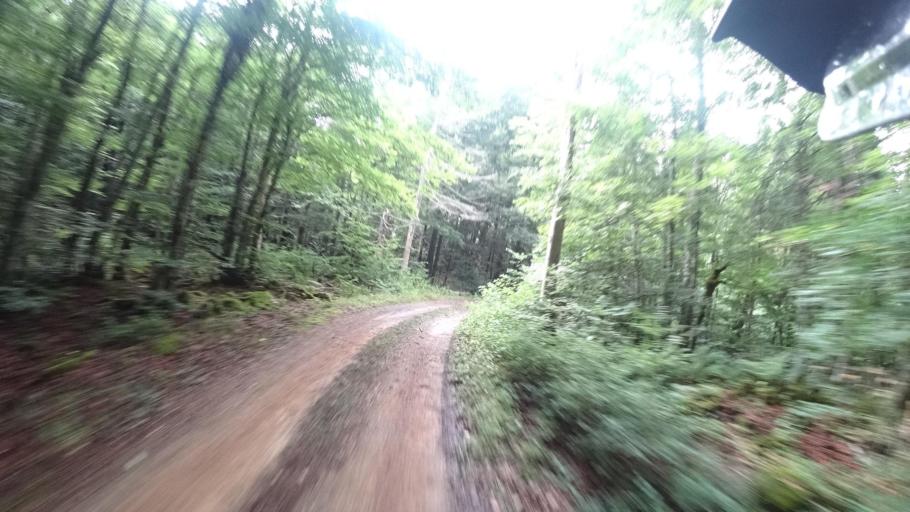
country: HR
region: Licko-Senjska
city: Jezerce
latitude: 44.7781
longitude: 15.6462
